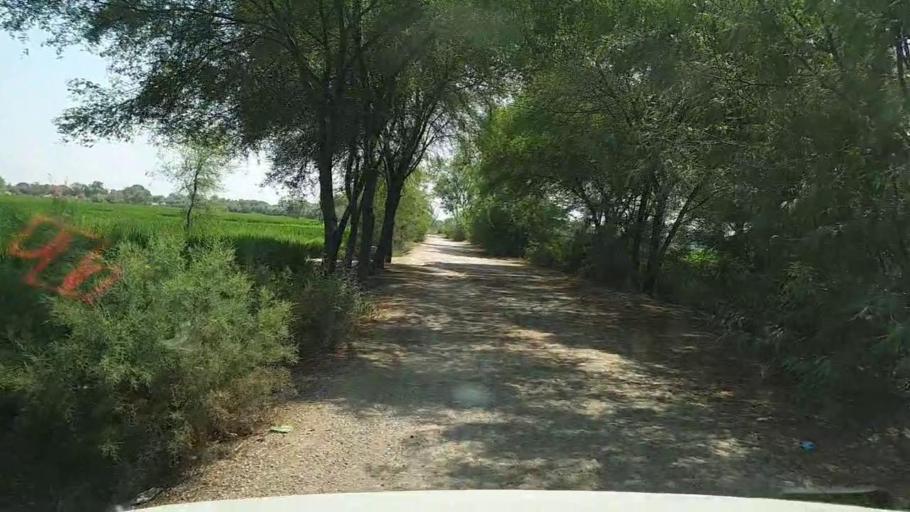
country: PK
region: Sindh
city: Kandhkot
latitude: 28.2714
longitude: 69.3594
